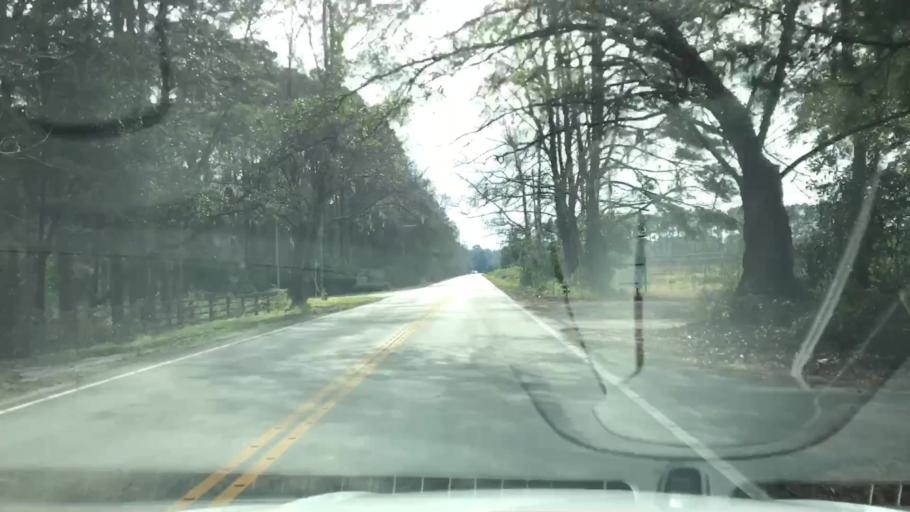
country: US
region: South Carolina
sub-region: Charleston County
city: Shell Point
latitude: 32.7249
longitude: -80.0236
